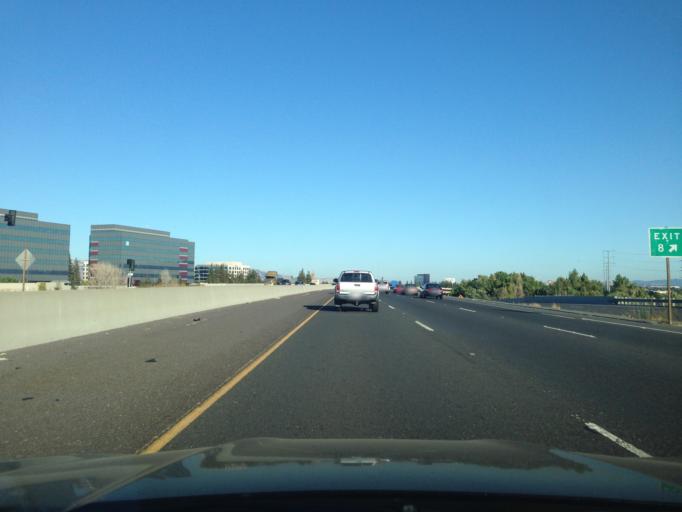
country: US
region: California
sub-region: Santa Clara County
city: Santa Clara
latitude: 37.3675
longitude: -121.9230
